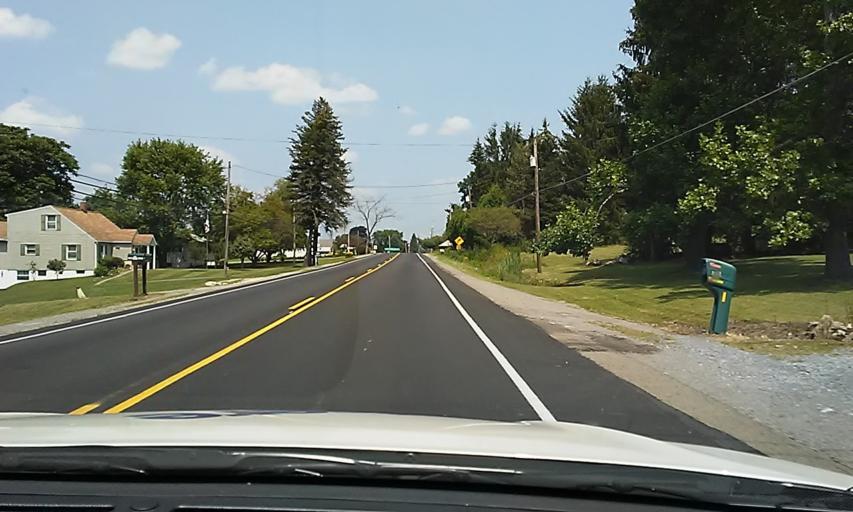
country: US
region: Pennsylvania
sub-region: Elk County
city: Saint Marys
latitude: 41.4406
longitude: -78.5052
